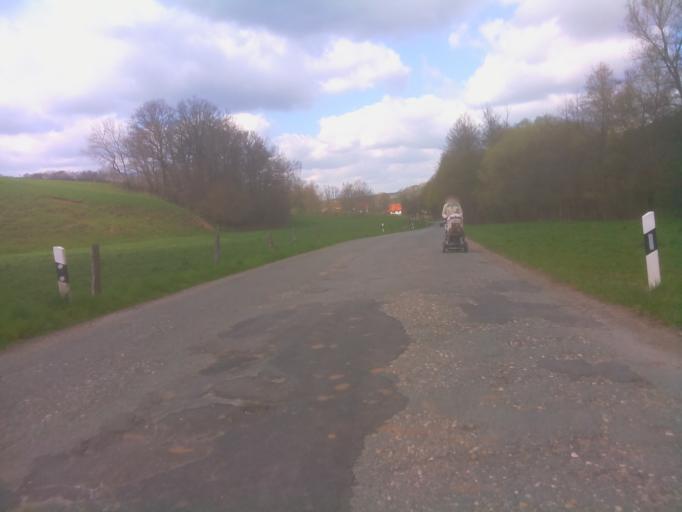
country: DE
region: Thuringia
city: Kleinebersdorf
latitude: 50.8097
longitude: 11.8463
